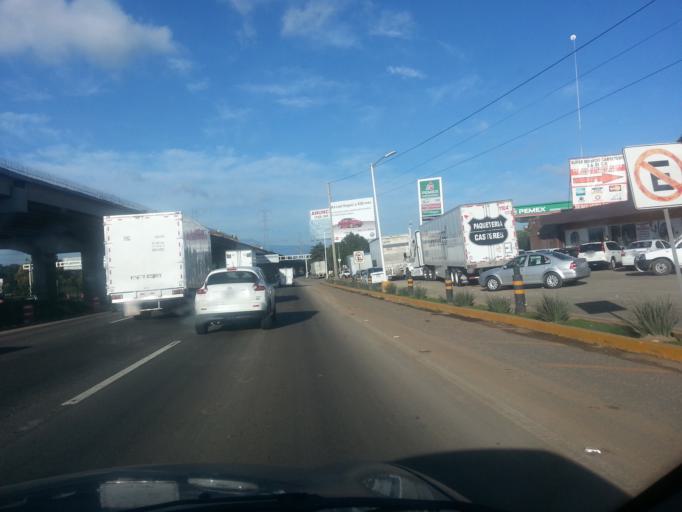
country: MX
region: Mexico
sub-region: Lerma
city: San Miguel Ameyalco
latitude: 19.2895
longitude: -99.4375
